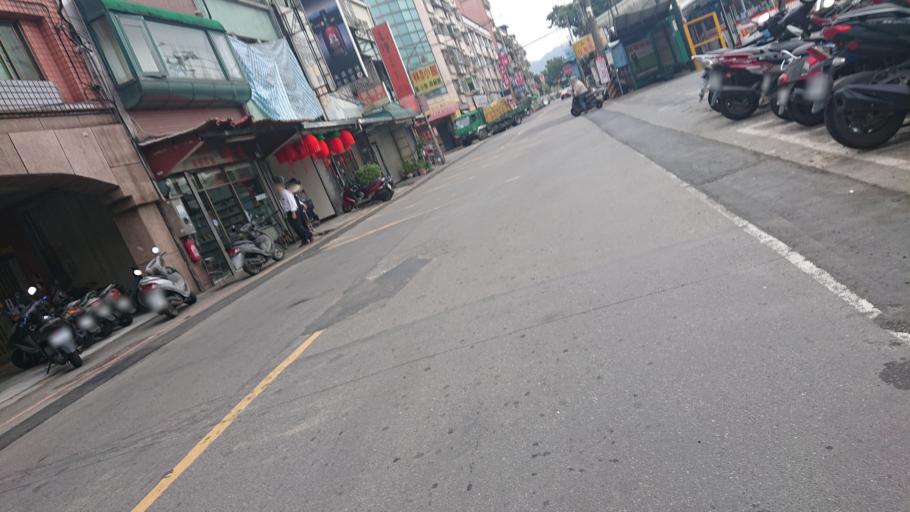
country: TW
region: Taiwan
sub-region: Taoyuan
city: Taoyuan
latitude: 24.9372
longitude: 121.3671
